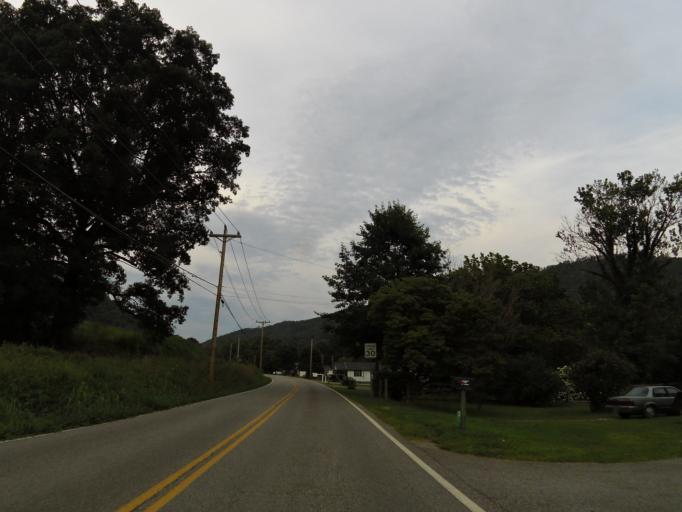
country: US
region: Tennessee
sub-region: Anderson County
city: Rocky Top
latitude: 36.1973
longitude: -84.1714
